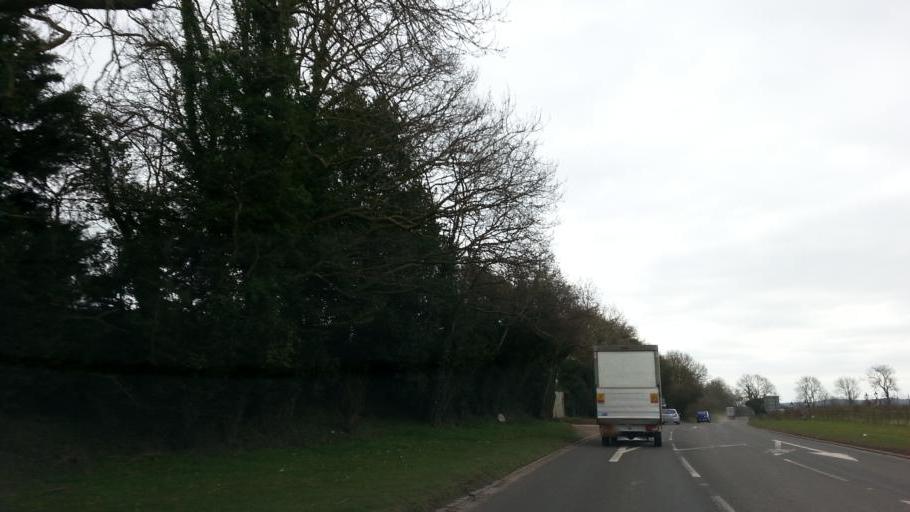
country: GB
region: England
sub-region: Staffordshire
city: Stone
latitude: 52.8866
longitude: -2.1212
